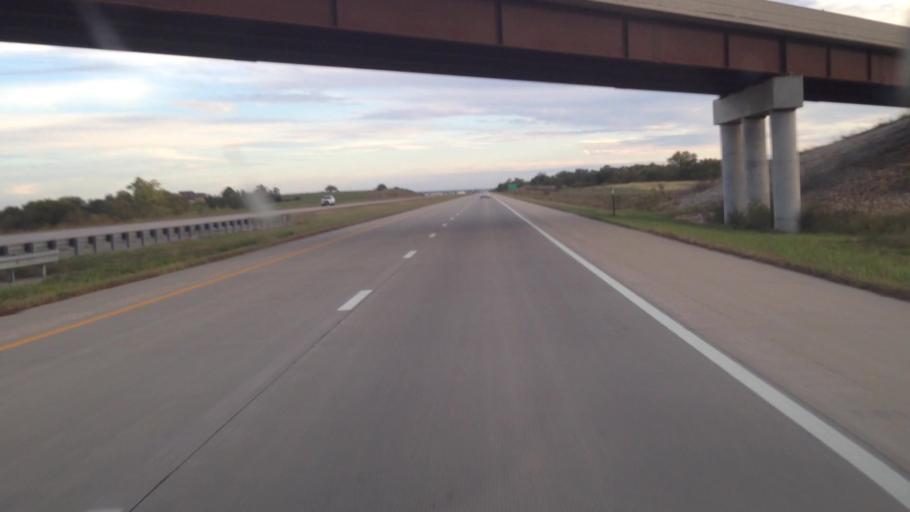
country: US
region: Kansas
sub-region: Franklin County
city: Ottawa
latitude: 38.6869
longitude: -95.2656
